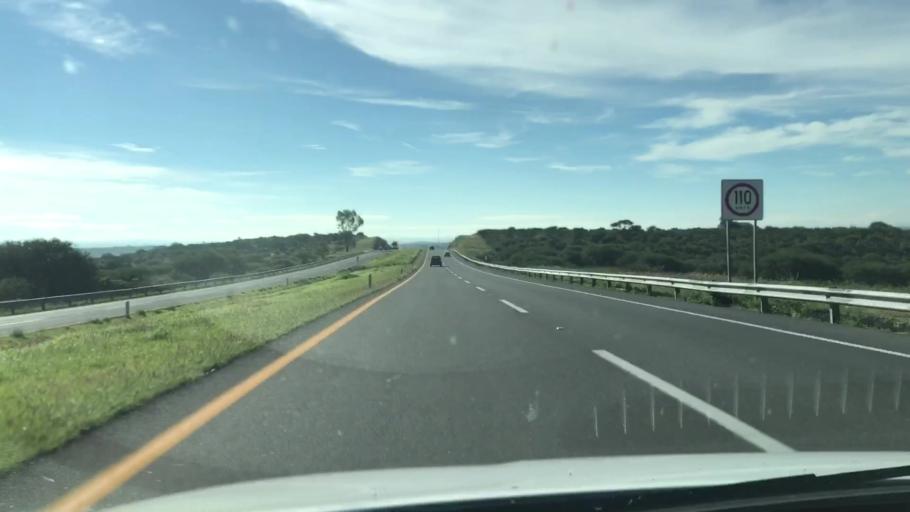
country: MX
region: Jalisco
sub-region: Union de San Antonio
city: San Jose del Caliche (El Caliche)
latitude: 21.2093
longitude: -101.9095
